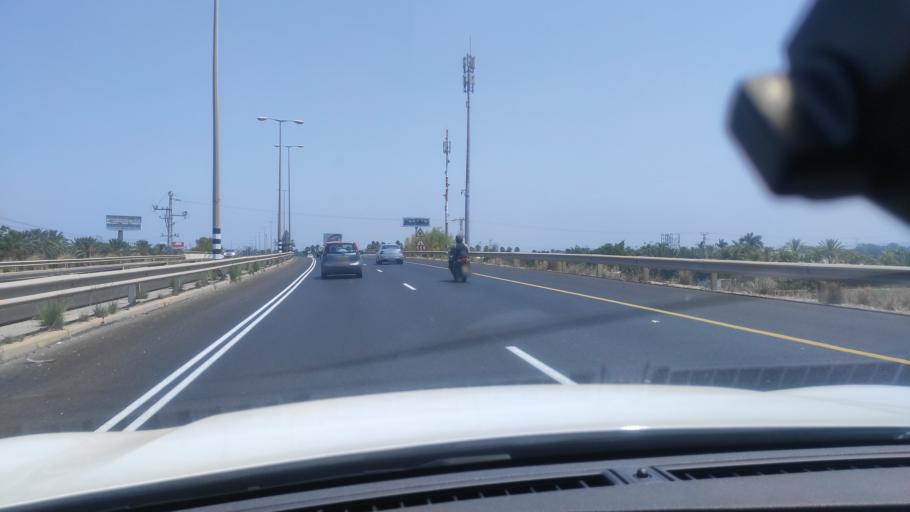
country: IL
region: Central District
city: Petah Tiqwa
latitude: 32.1105
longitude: 34.9023
